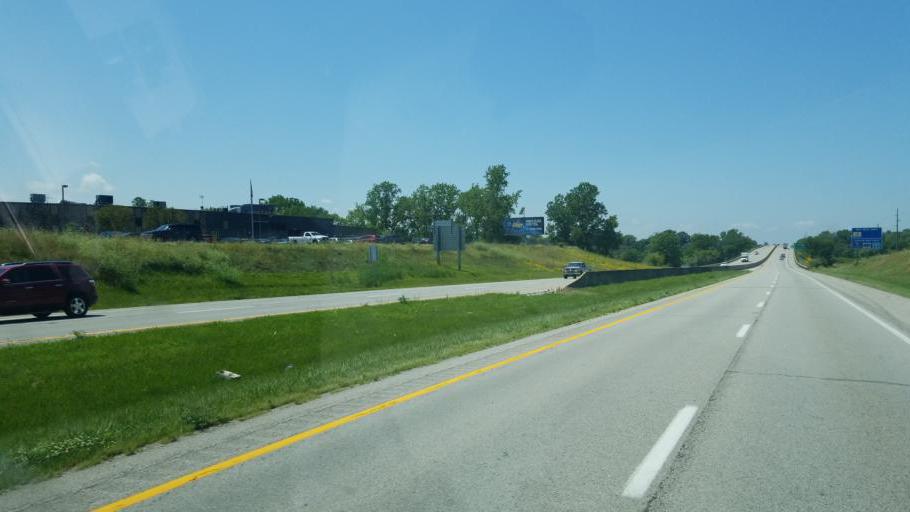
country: US
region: Ohio
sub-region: Sandusky County
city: Fremont
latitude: 41.3661
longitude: -83.0983
